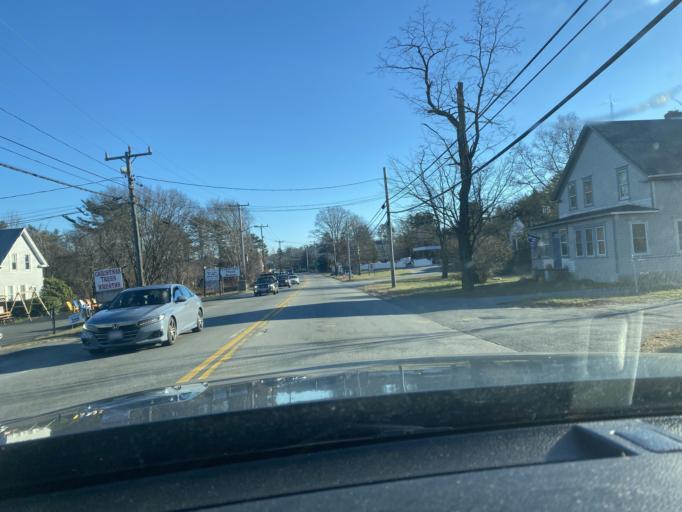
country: US
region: Massachusetts
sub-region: Plymouth County
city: Wareham Center
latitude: 41.7713
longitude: -70.7345
